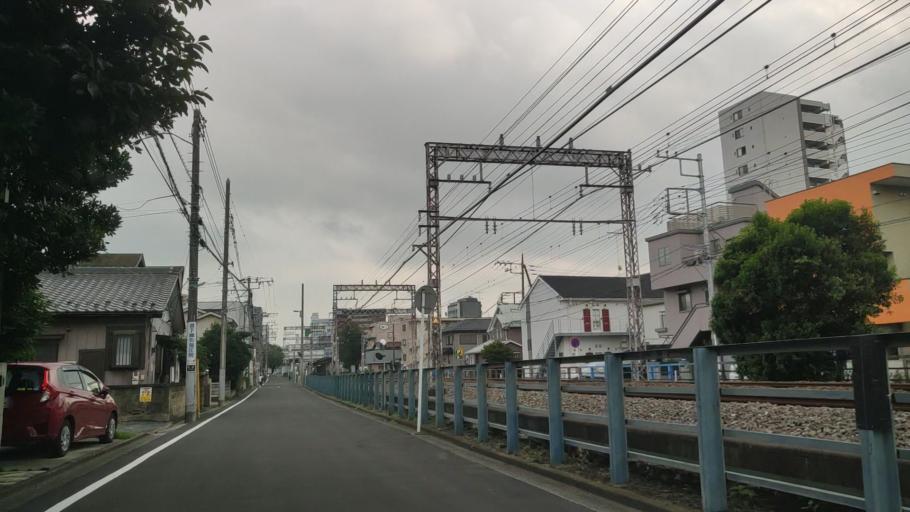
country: JP
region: Kanagawa
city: Minami-rinkan
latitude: 35.4927
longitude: 139.4497
